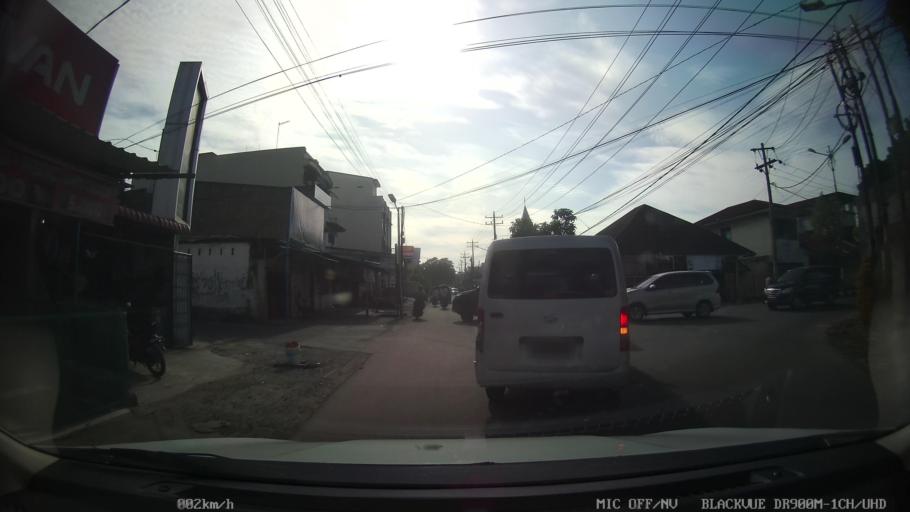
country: ID
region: North Sumatra
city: Medan
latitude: 3.6026
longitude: 98.6612
